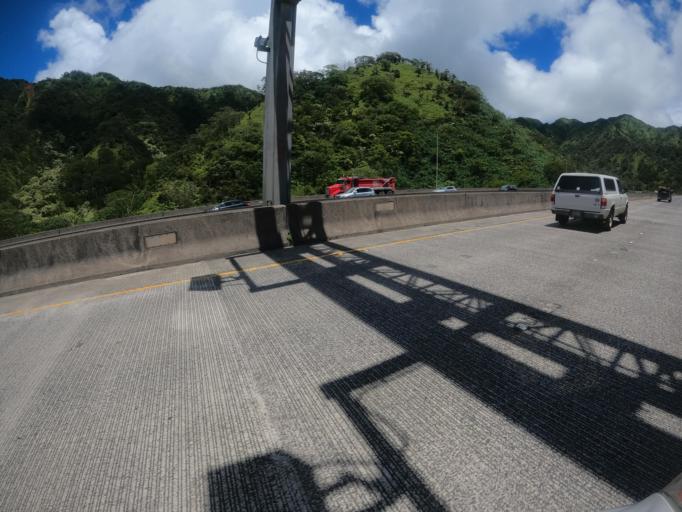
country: US
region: Hawaii
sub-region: Honolulu County
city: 'Ahuimanu
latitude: 21.4063
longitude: -157.8577
